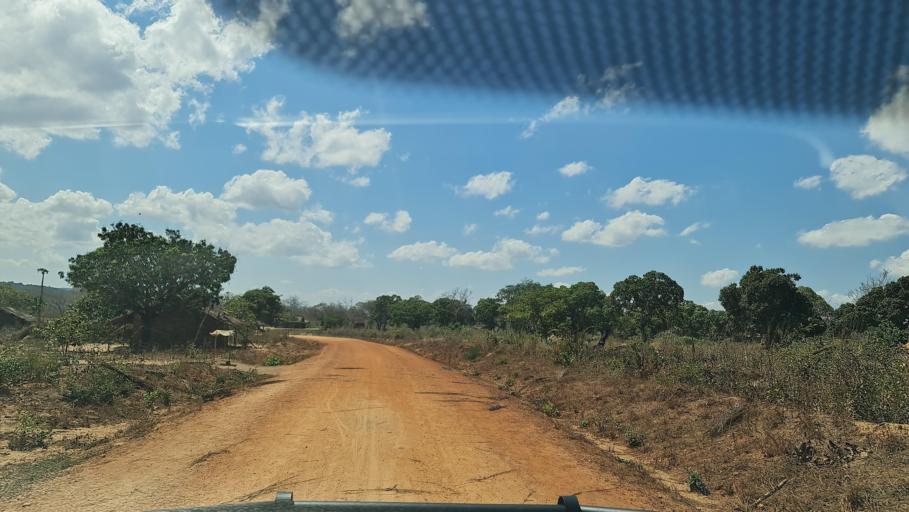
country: MZ
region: Nampula
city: Nacala
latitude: -14.1795
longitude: 40.2217
